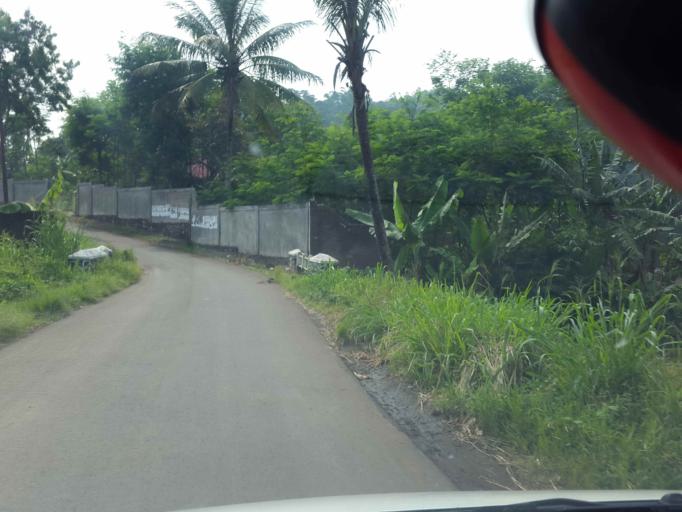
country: ID
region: West Java
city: Sukabumi
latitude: -6.9158
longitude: 106.9986
